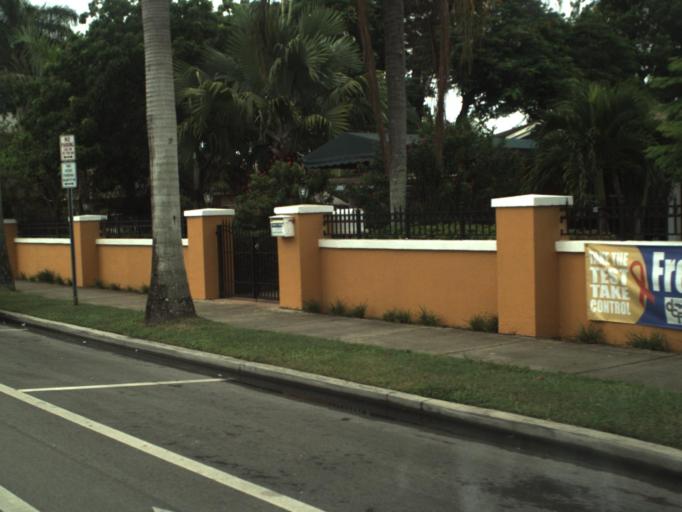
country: US
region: Florida
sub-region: Miami-Dade County
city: Homestead
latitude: 25.4807
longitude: -80.4775
